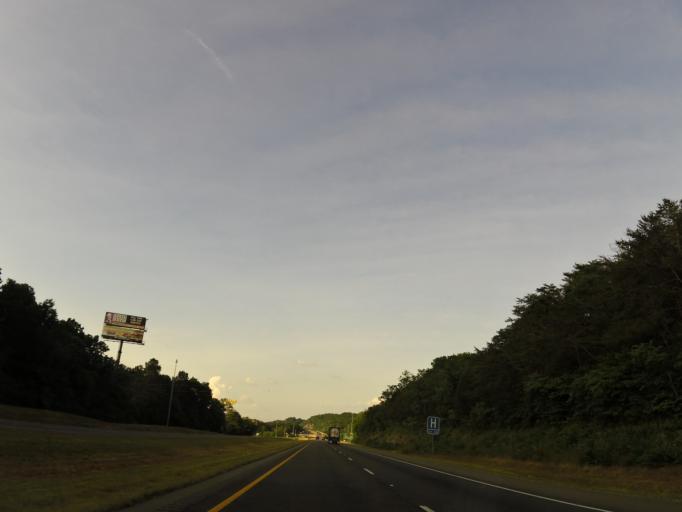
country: US
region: Alabama
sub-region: DeKalb County
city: Fort Payne
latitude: 34.4326
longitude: -85.7544
